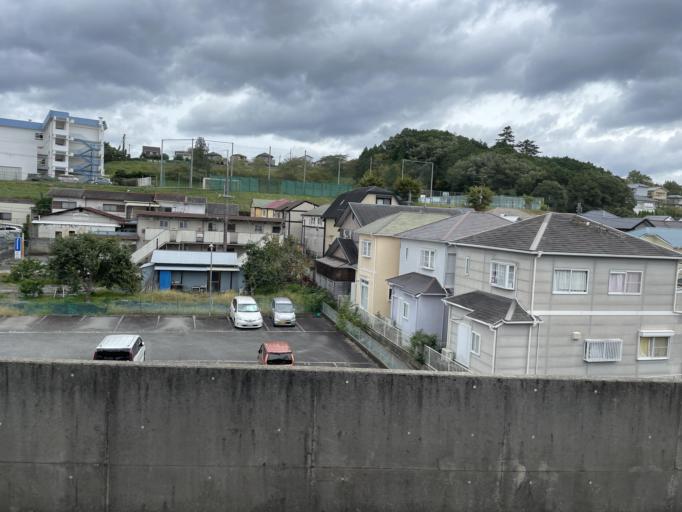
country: JP
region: Osaka
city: Ikeda
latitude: 34.8914
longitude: 135.4112
